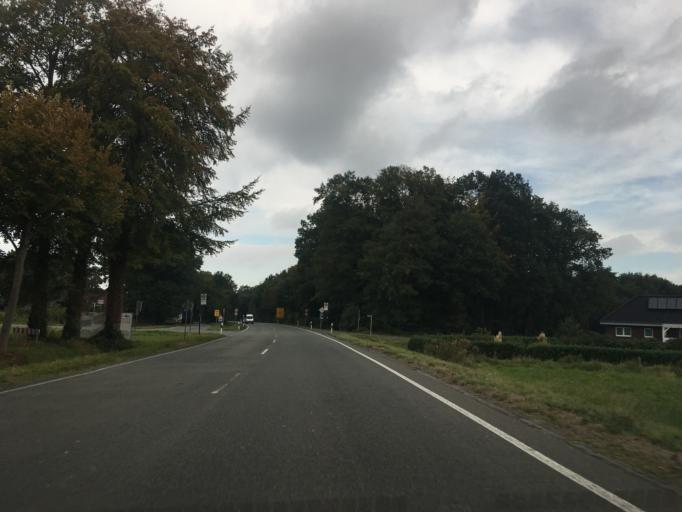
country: DE
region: North Rhine-Westphalia
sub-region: Regierungsbezirk Munster
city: Schoppingen
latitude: 52.1012
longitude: 7.2074
